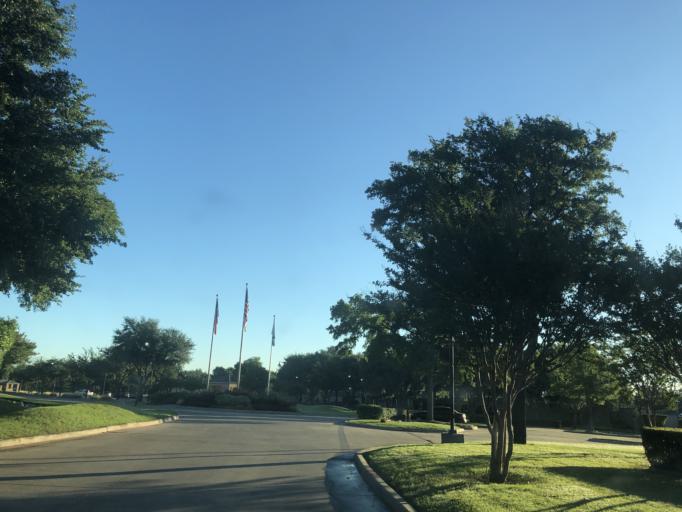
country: US
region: Texas
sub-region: Dallas County
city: Garland
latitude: 32.8397
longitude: -96.6456
